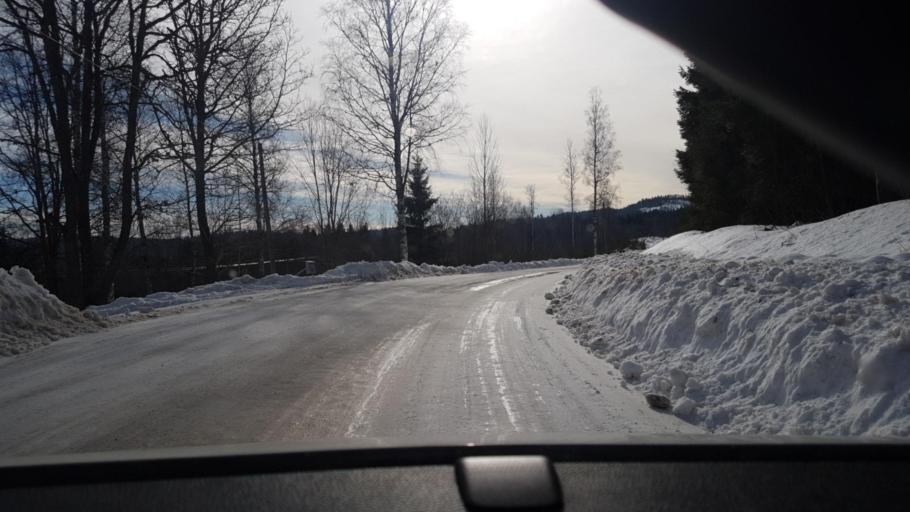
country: NO
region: Ostfold
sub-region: Romskog
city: Romskog
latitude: 59.8249
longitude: 11.9697
